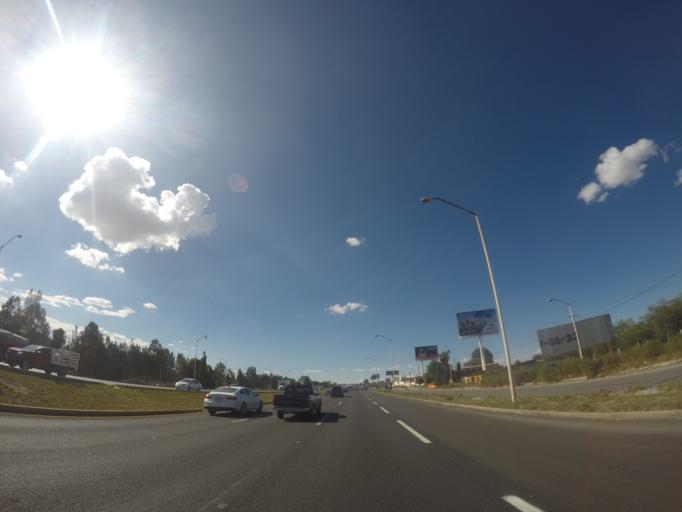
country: MX
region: San Luis Potosi
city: La Pila
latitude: 22.0761
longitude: -100.8740
